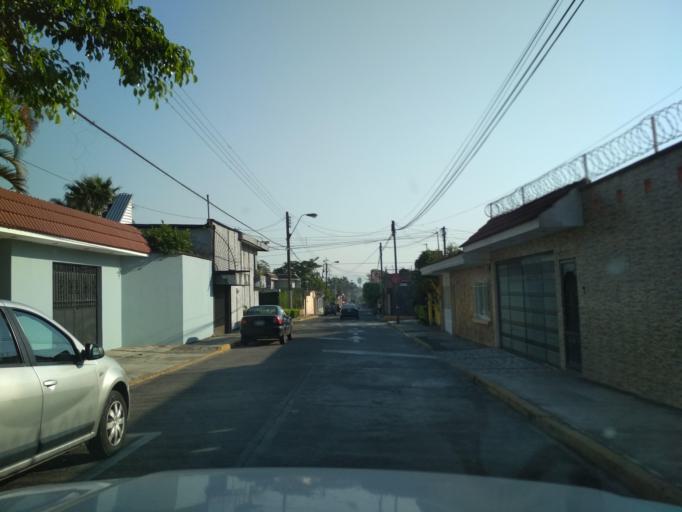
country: MX
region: Veracruz
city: Ixtac Zoquitlan
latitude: 18.8578
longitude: -97.0767
